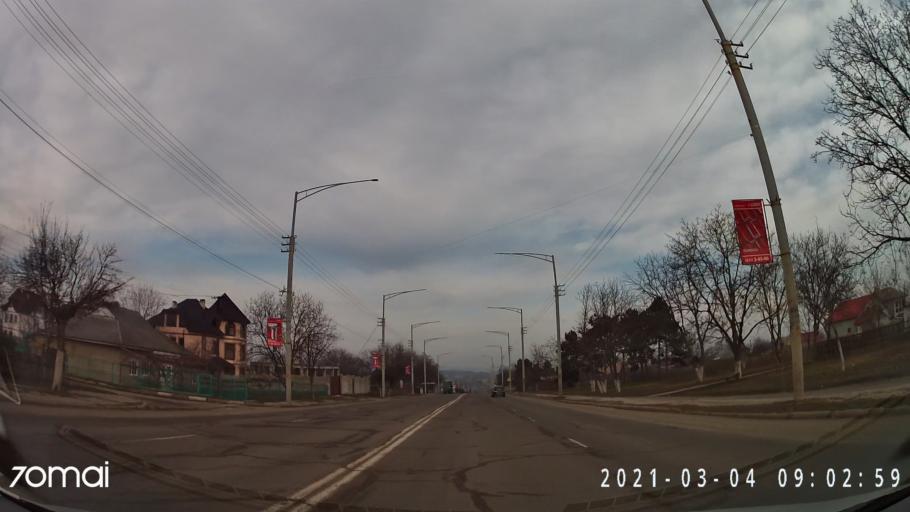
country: MD
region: Balti
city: Balti
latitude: 47.7458
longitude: 27.9489
